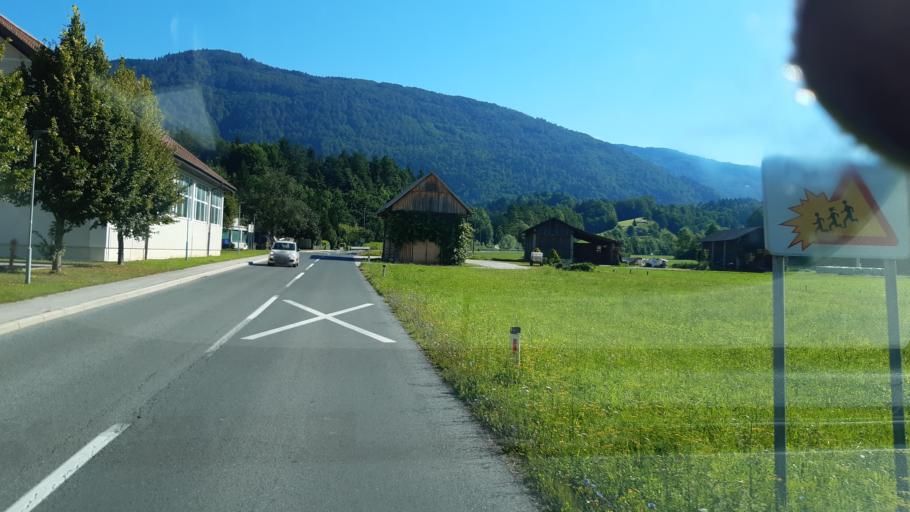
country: SI
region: Lukovica
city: Lukovica pri Domzalah
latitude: 46.2159
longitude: 14.7357
